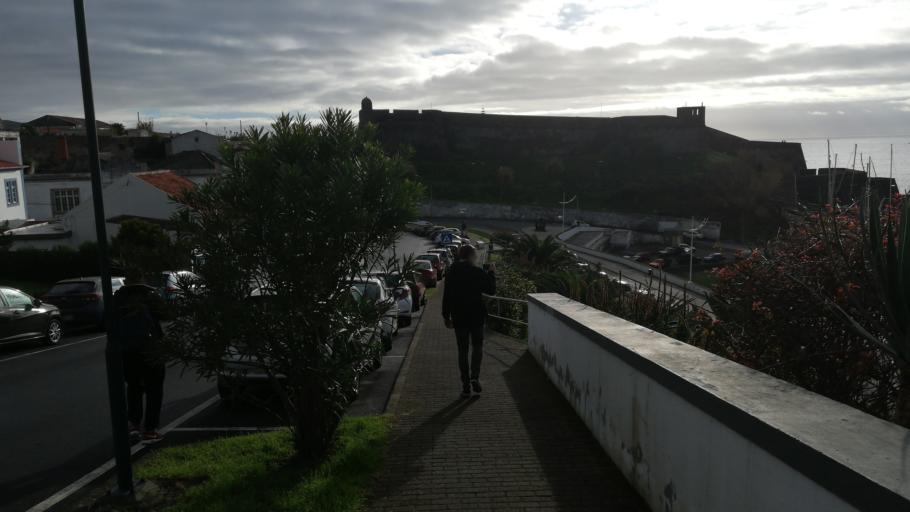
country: PT
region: Azores
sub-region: Angra do Heroismo
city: Angra do Heroismo
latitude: 38.6529
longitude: -27.2142
